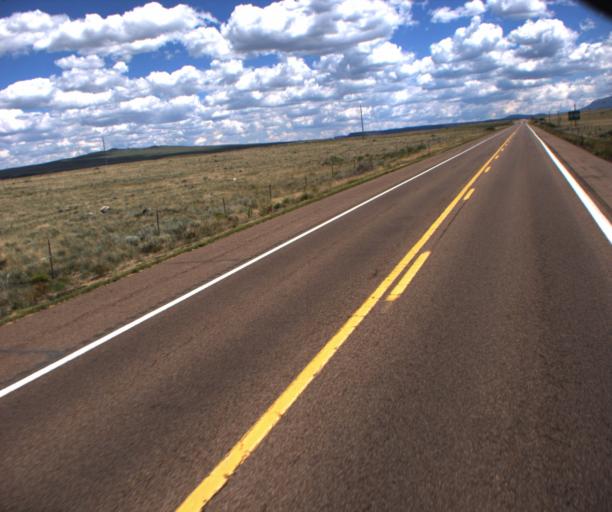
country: US
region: Arizona
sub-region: Apache County
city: Springerville
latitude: 34.1800
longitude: -109.3258
